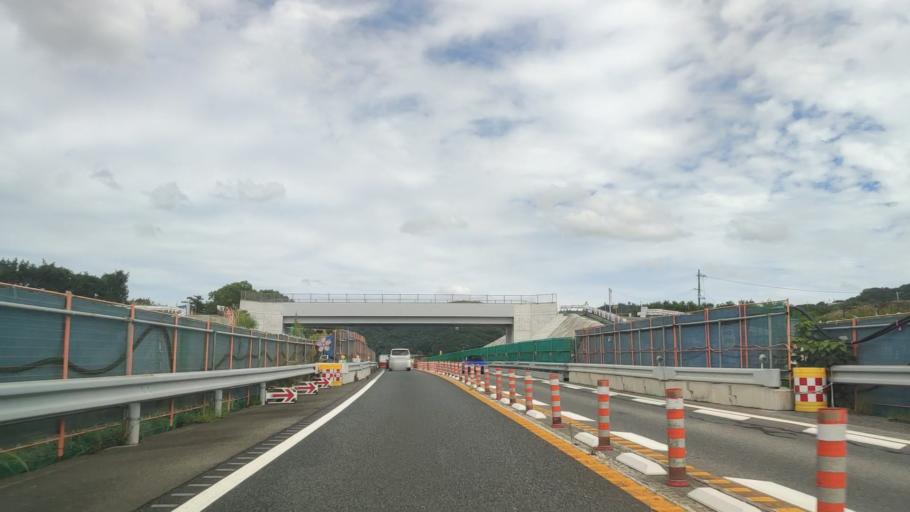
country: JP
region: Wakayama
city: Gobo
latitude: 33.9084
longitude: 135.1939
